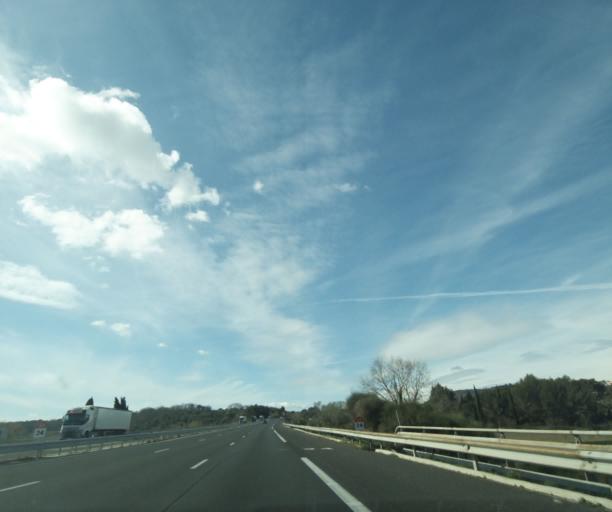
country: FR
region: Languedoc-Roussillon
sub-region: Departement du Gard
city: Sernhac
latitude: 43.9073
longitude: 4.5602
